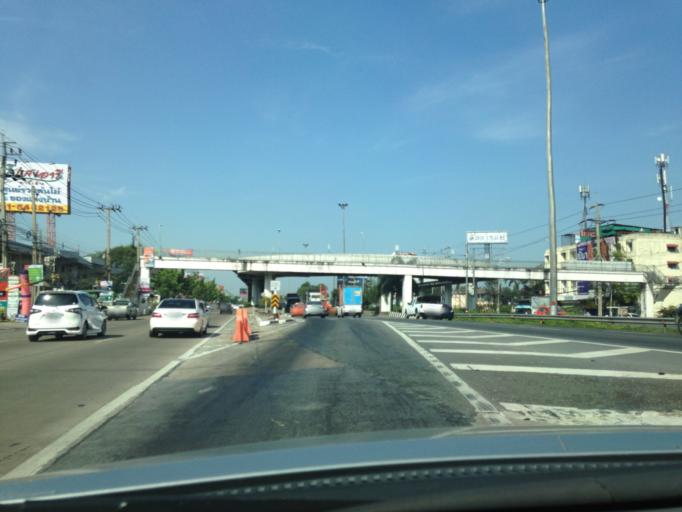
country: TH
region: Nonthaburi
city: Bang Yai
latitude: 13.8294
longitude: 100.4129
